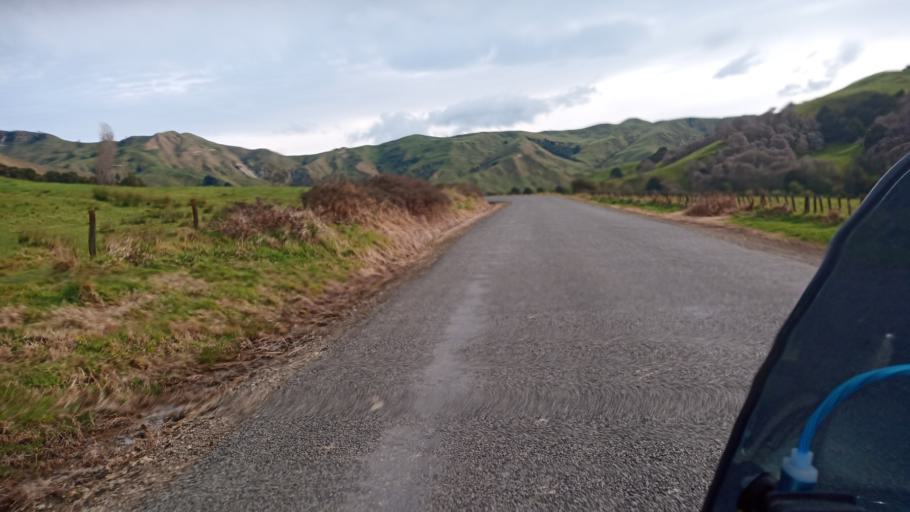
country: NZ
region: Hawke's Bay
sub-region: Wairoa District
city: Wairoa
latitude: -38.7956
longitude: 177.4466
